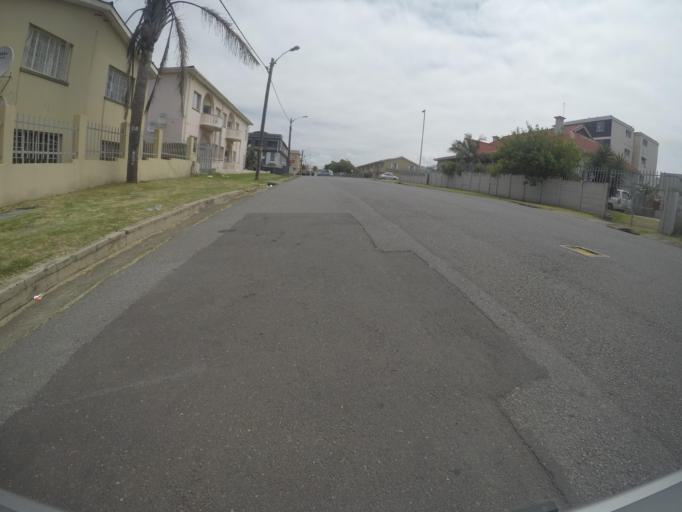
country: ZA
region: Eastern Cape
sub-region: Buffalo City Metropolitan Municipality
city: East London
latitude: -33.0207
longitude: 27.9149
